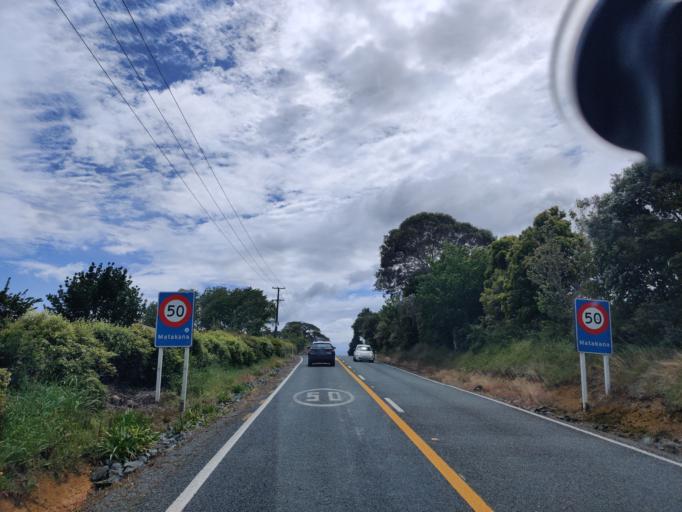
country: NZ
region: Auckland
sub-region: Auckland
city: Warkworth
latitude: -36.3598
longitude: 174.7101
